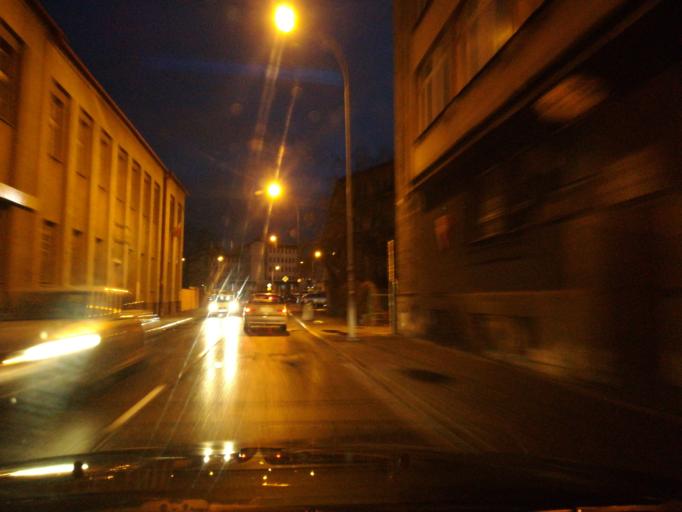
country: PL
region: Subcarpathian Voivodeship
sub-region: Rzeszow
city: Rzeszow
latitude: 50.0411
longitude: 22.0088
